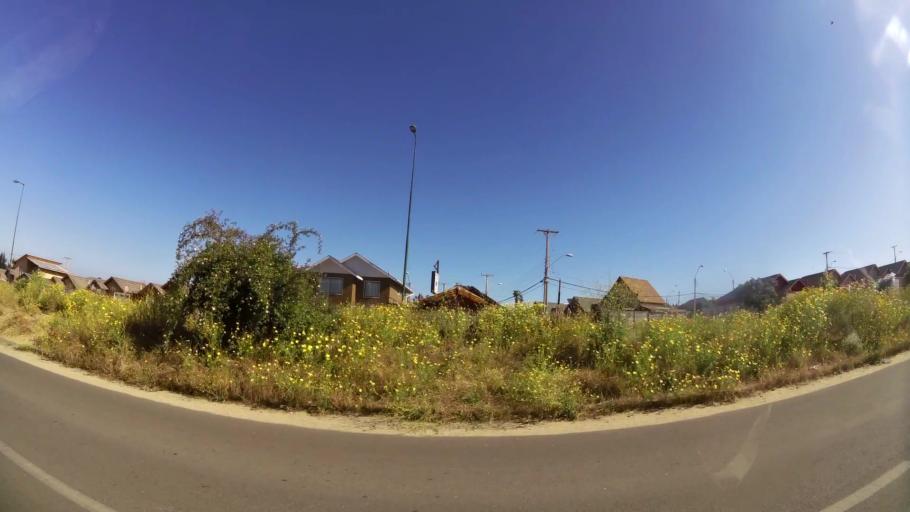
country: CL
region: Valparaiso
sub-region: Provincia de Valparaiso
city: Valparaiso
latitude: -33.1202
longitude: -71.5820
